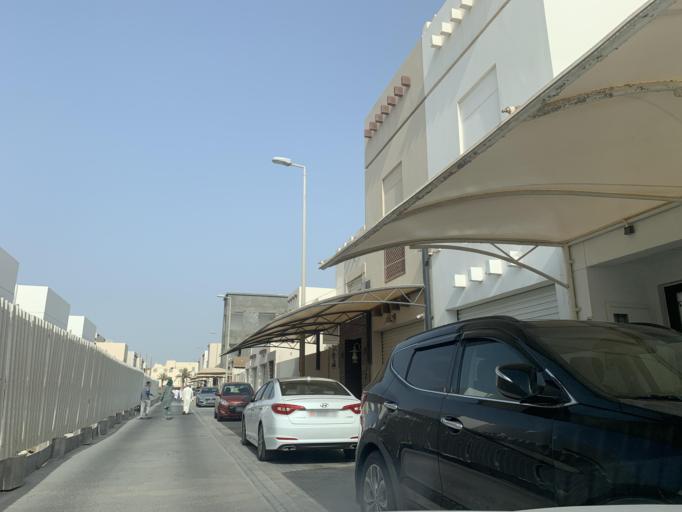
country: BH
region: Manama
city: Jidd Hafs
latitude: 26.2260
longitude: 50.4400
